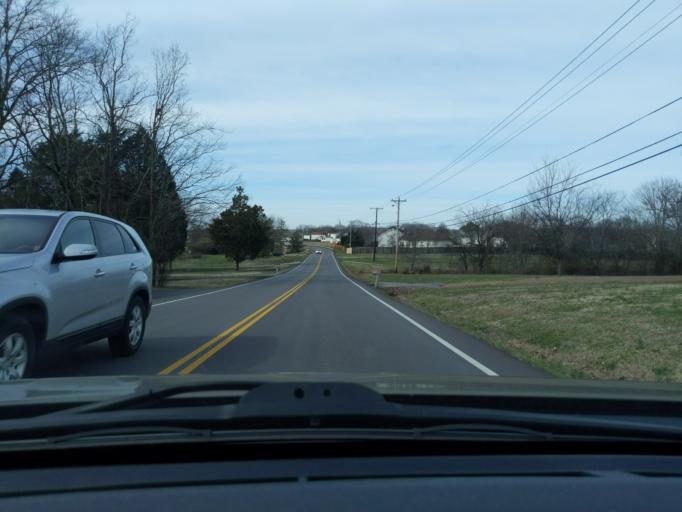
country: US
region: Tennessee
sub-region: Wilson County
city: Rural Hill
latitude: 36.1661
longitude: -86.4626
